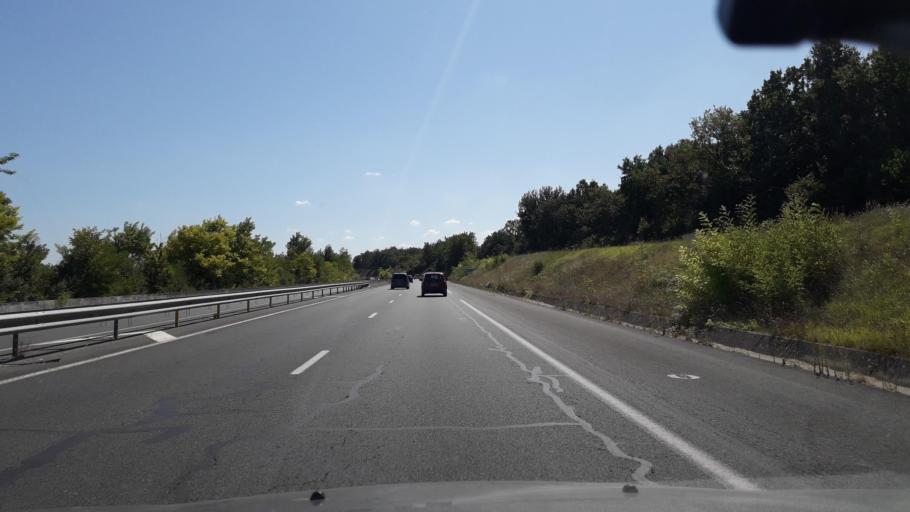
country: FR
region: Poitou-Charentes
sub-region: Departement de la Charente
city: Saint-Yrieix-sur-Charente
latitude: 45.6820
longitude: 0.1207
